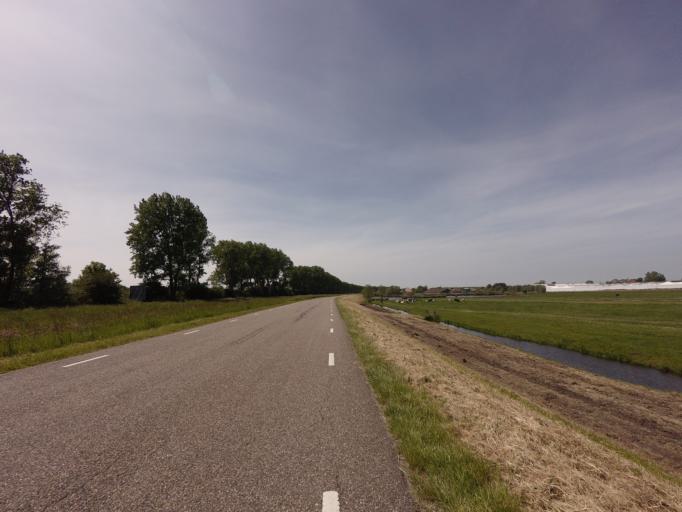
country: NL
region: North Holland
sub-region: Gemeente Velsen
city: Velsen-Zuid
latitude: 52.4364
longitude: 4.7224
